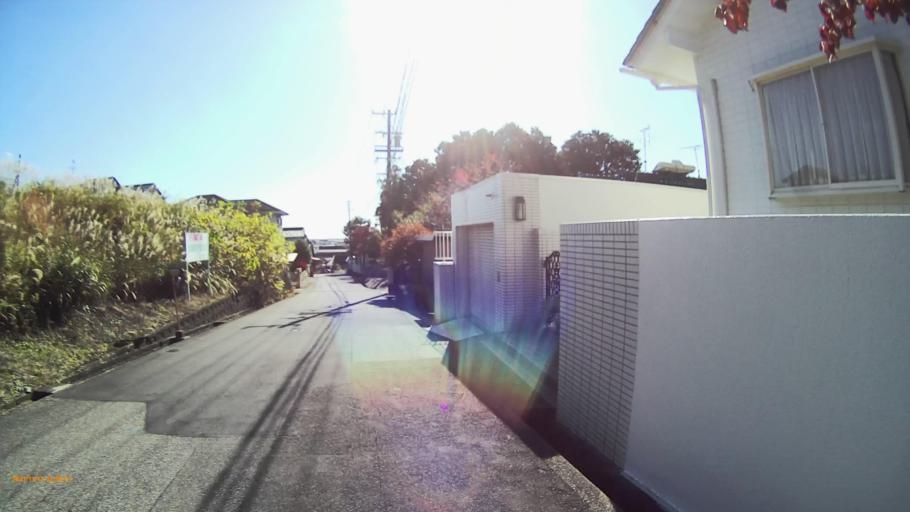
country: JP
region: Gifu
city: Inuyama
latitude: 35.4051
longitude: 136.9435
